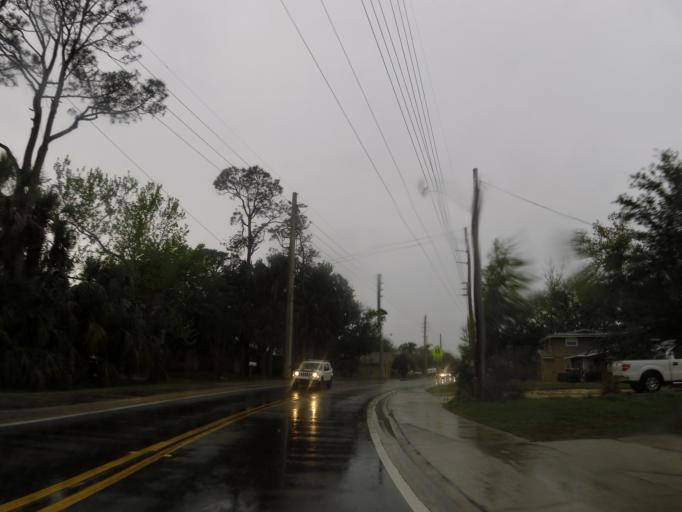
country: US
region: Florida
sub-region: Duval County
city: Jacksonville Beach
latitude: 30.2710
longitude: -81.3949
